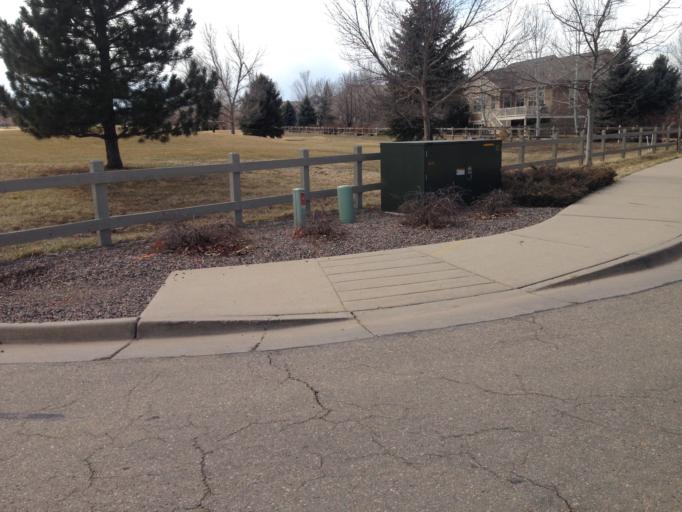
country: US
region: Colorado
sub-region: Boulder County
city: Louisville
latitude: 40.0073
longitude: -105.1356
